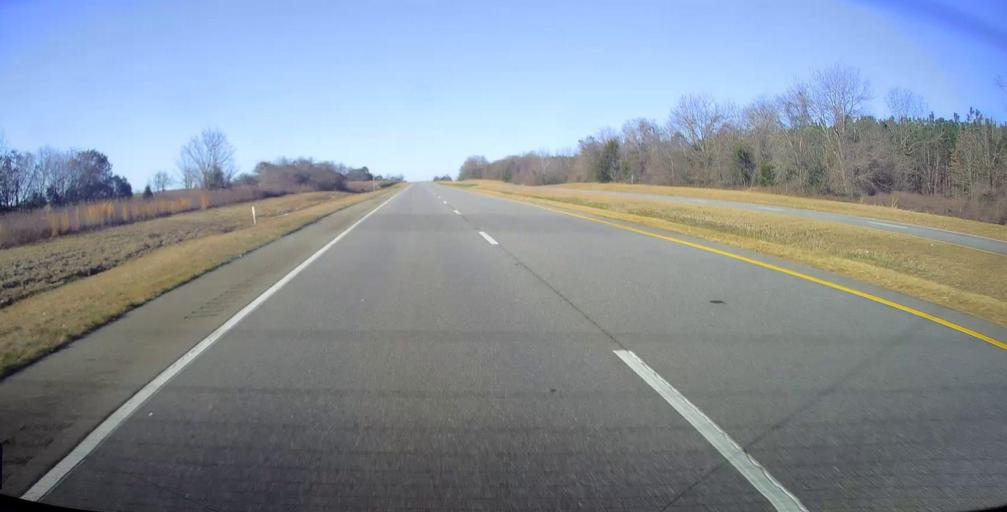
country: US
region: Georgia
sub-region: Sumter County
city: Americus
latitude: 31.9407
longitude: -84.2556
